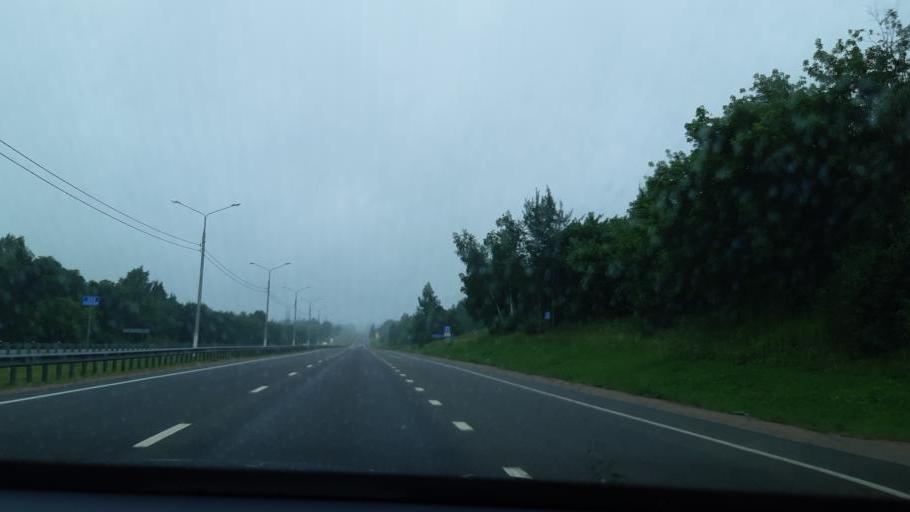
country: RU
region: Smolensk
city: Talashkino
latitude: 54.6507
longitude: 32.1681
